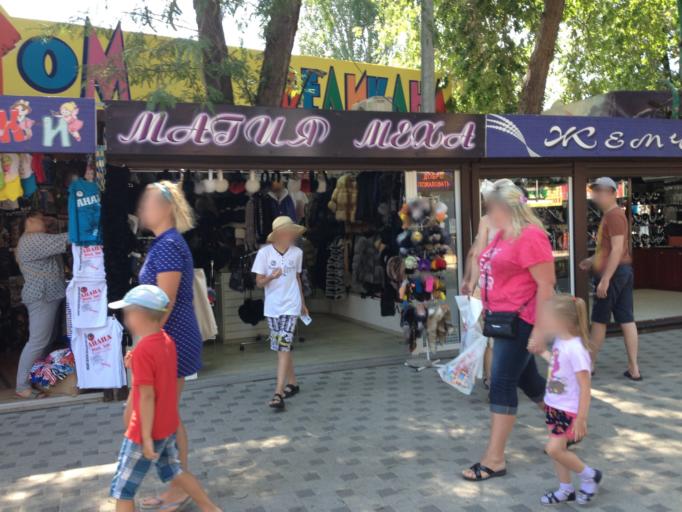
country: RU
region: Krasnodarskiy
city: Anapa
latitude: 44.8967
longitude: 37.3145
